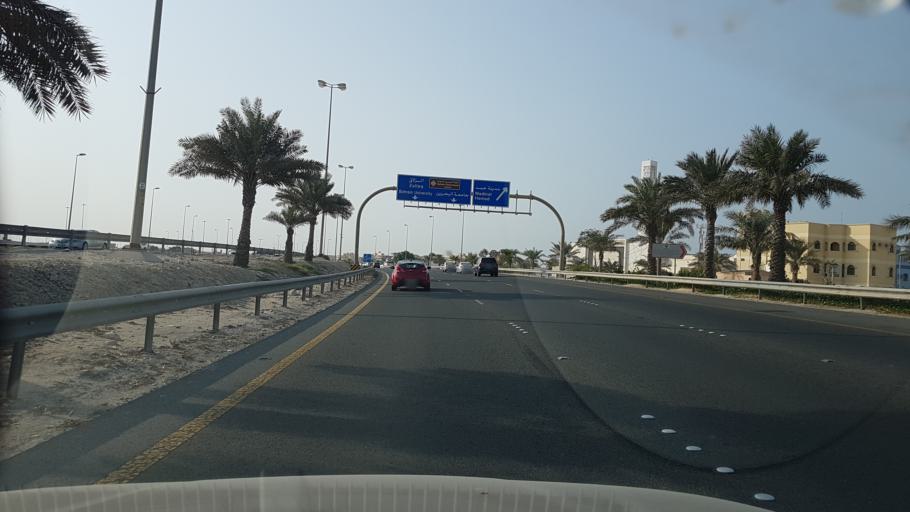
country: BH
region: Central Governorate
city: Madinat Hamad
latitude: 26.1275
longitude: 50.5061
